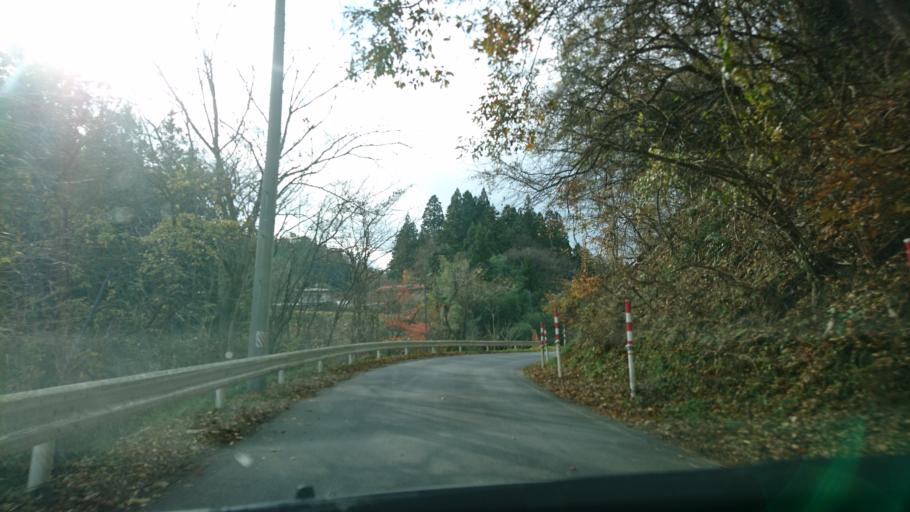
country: JP
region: Iwate
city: Ichinoseki
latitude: 39.0082
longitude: 141.2324
